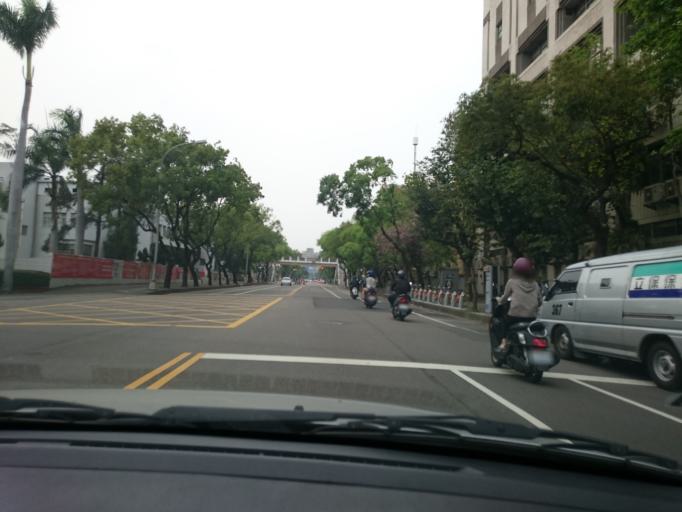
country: TW
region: Taiwan
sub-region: Taichung City
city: Taichung
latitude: 24.1564
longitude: 120.6344
